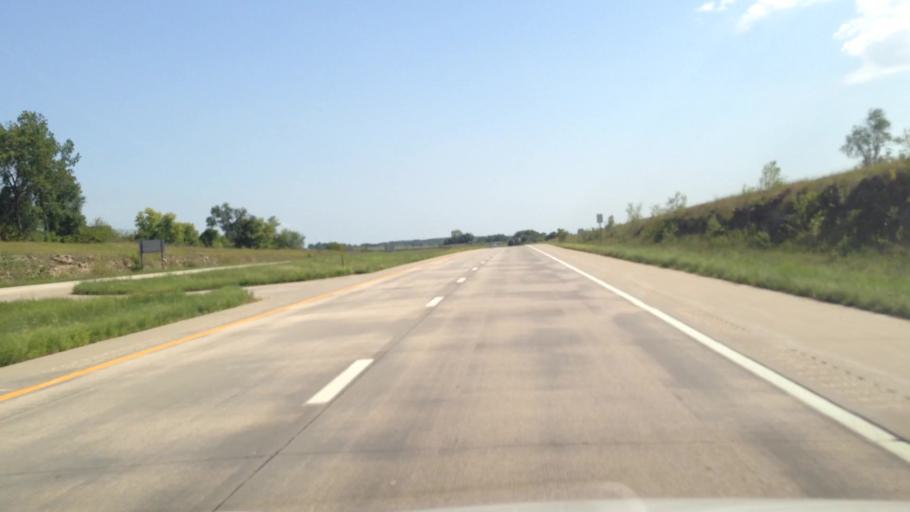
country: US
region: Kansas
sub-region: Miami County
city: Louisburg
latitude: 38.5572
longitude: -94.6918
